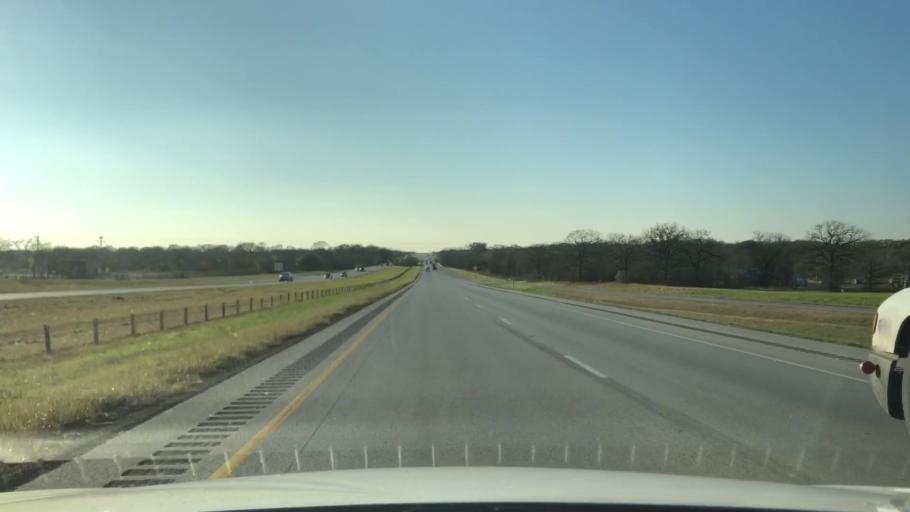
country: US
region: Texas
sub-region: Fayette County
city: Flatonia
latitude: 29.6921
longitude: -97.1788
